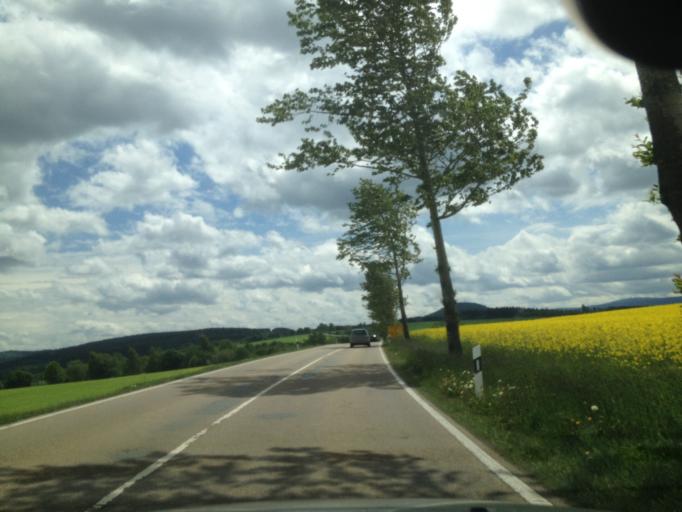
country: DE
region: Saxony
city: Annaberg-Buchholz
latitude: 50.5534
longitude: 13.0170
